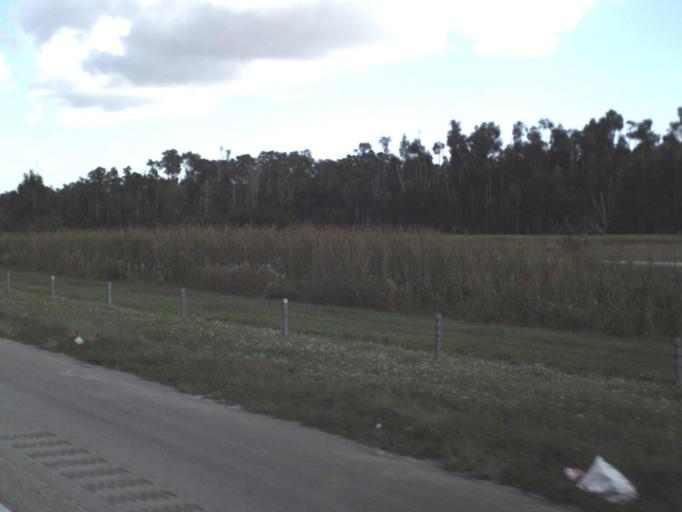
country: US
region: Florida
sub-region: Palm Beach County
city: Plantation Mobile Home Park
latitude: 26.7246
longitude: -80.1355
